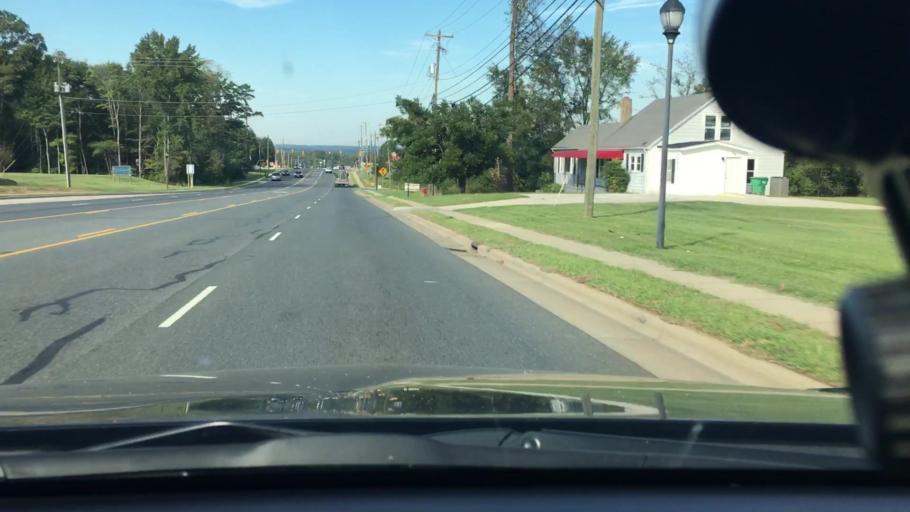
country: US
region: North Carolina
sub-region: Stanly County
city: Locust
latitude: 35.2546
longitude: -80.4480
